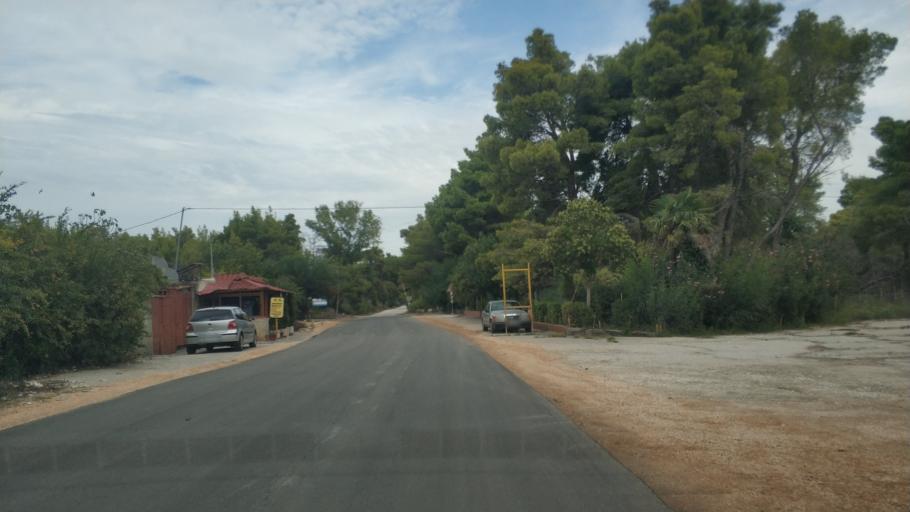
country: AL
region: Vlore
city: Vlore
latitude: 40.4779
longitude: 19.4521
